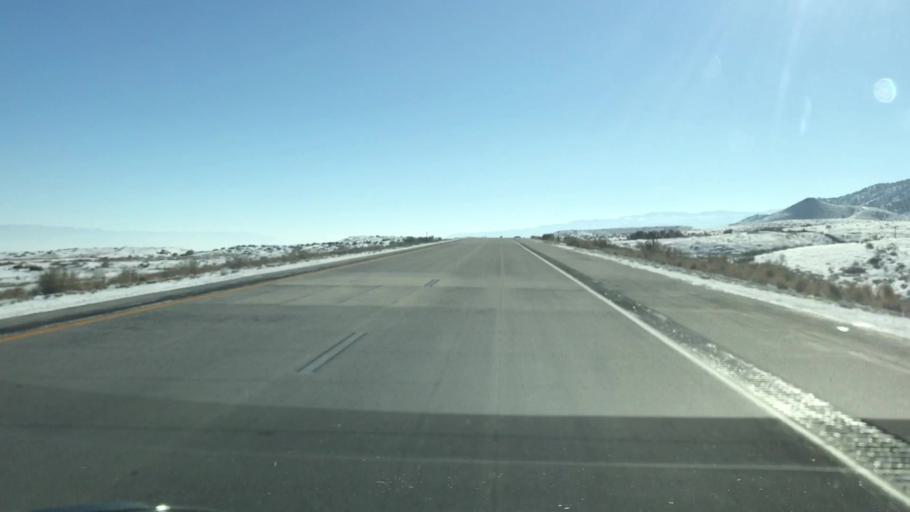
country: US
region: Colorado
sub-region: Mesa County
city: Loma
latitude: 39.1976
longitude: -108.8480
